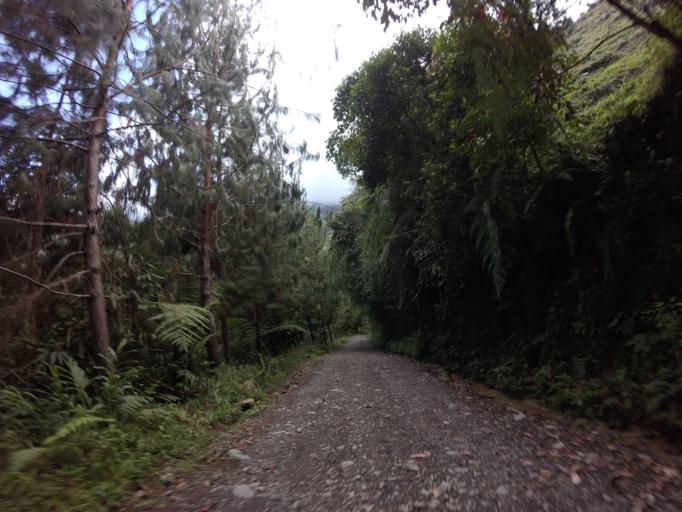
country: CO
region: Caldas
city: Pensilvania
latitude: 5.4525
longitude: -75.1581
